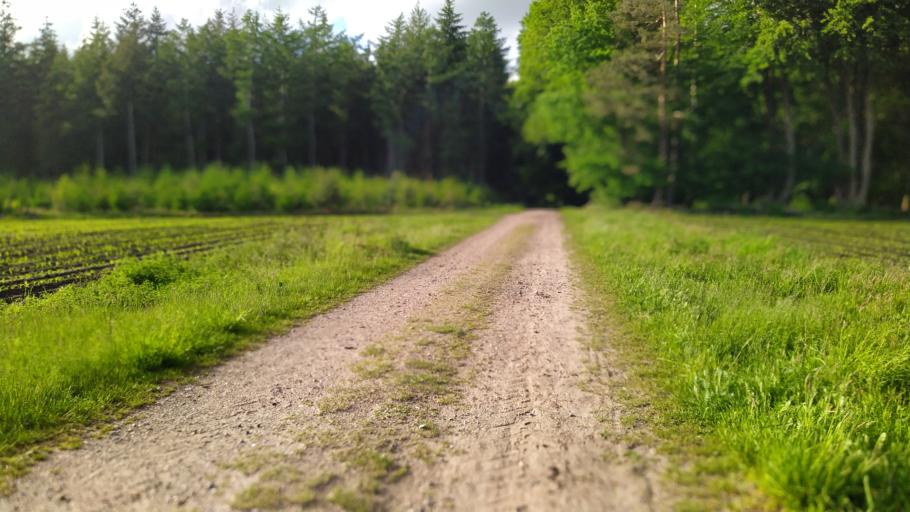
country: DE
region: Lower Saxony
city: Farven
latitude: 53.4385
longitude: 9.2868
